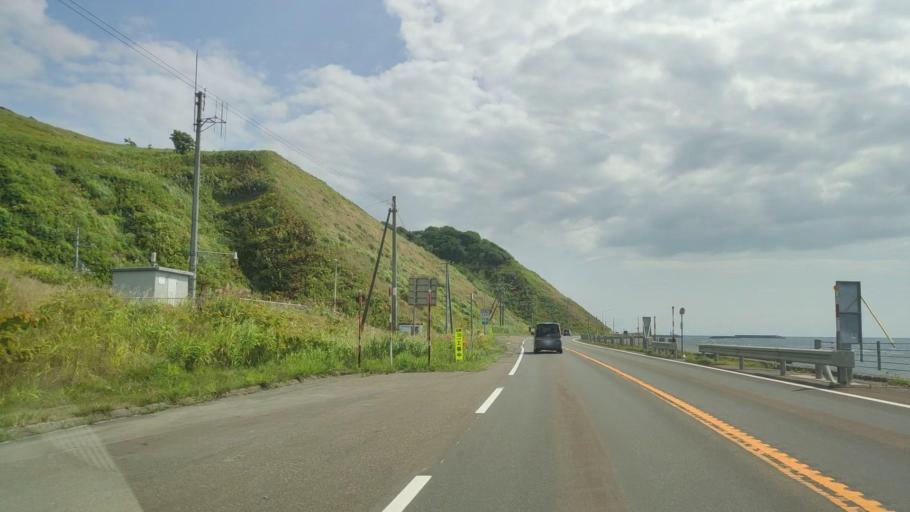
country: JP
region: Hokkaido
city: Rumoi
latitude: 44.2364
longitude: 141.6571
